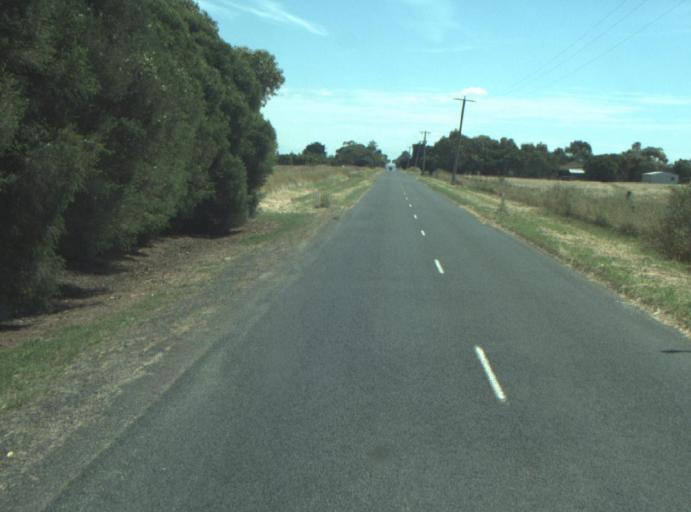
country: AU
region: Victoria
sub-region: Greater Geelong
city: Leopold
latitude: -38.1701
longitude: 144.4543
